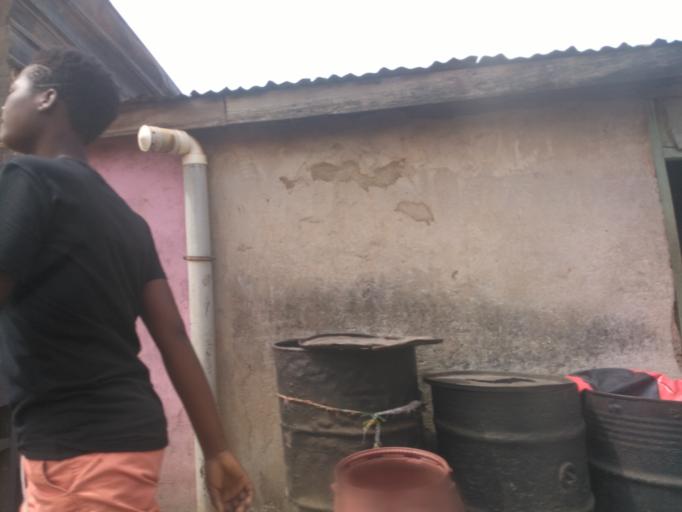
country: GH
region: Ashanti
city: Kumasi
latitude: 6.7008
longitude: -1.6106
